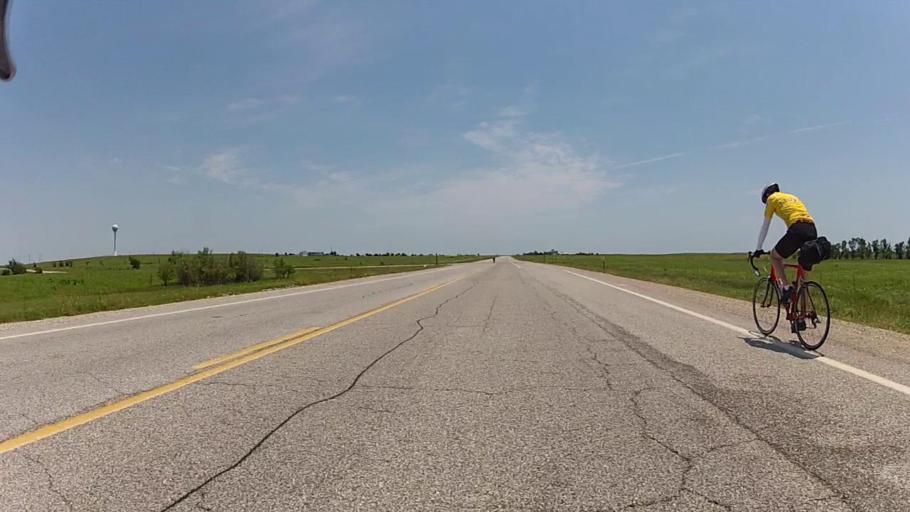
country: US
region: Kansas
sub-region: Chautauqua County
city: Sedan
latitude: 37.1077
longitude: -96.2493
